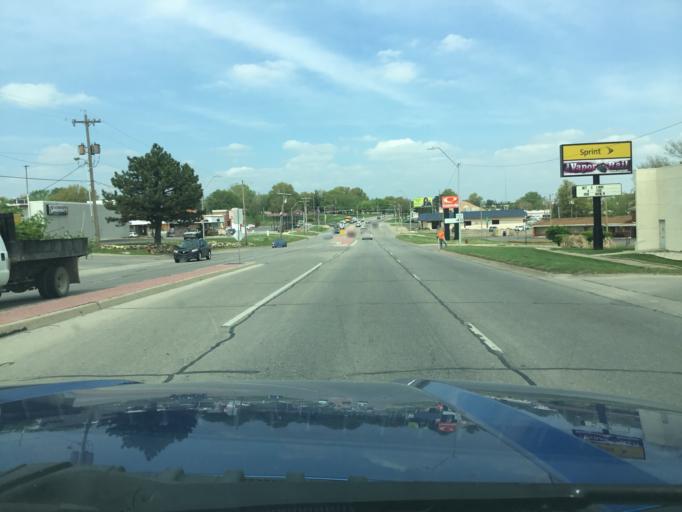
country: US
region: Kansas
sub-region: Shawnee County
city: Topeka
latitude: 39.0125
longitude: -95.6876
